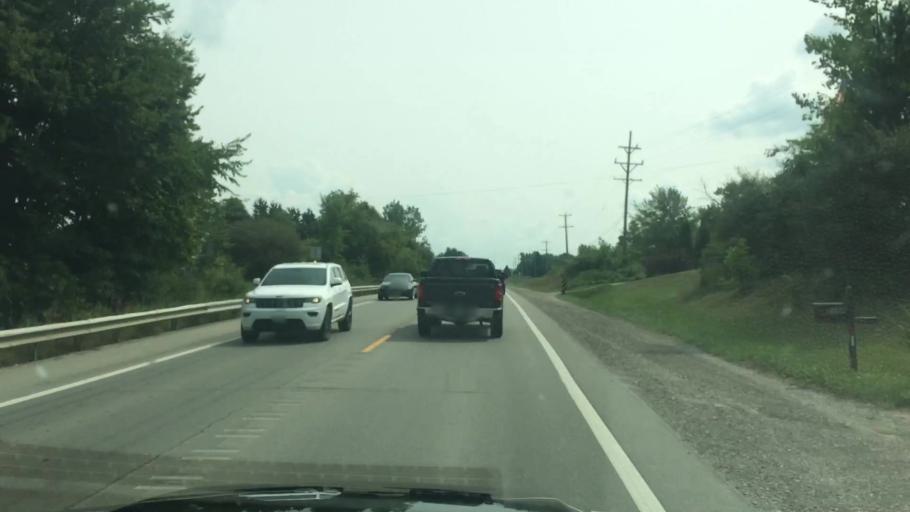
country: US
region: Michigan
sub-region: Oakland County
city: Oxford
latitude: 42.9093
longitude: -83.3123
